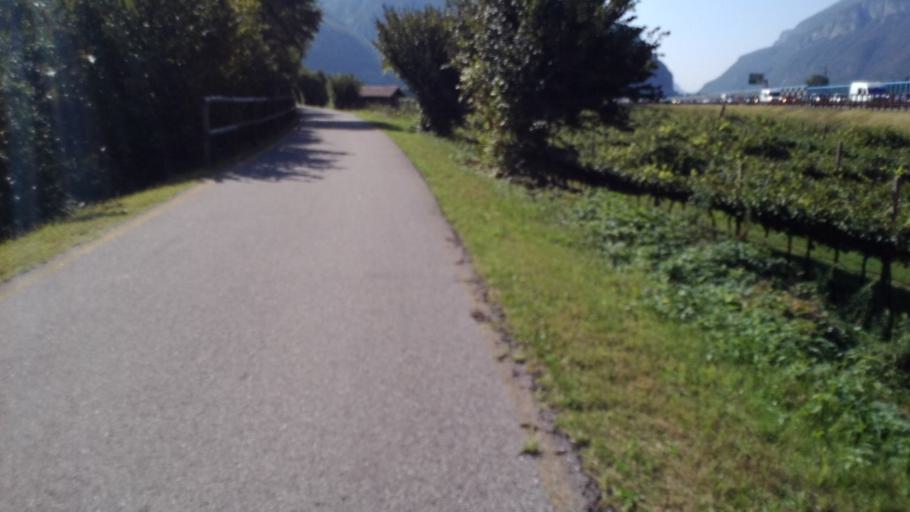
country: IT
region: Trentino-Alto Adige
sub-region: Provincia di Trento
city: Avio
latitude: 45.7083
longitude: 10.9263
